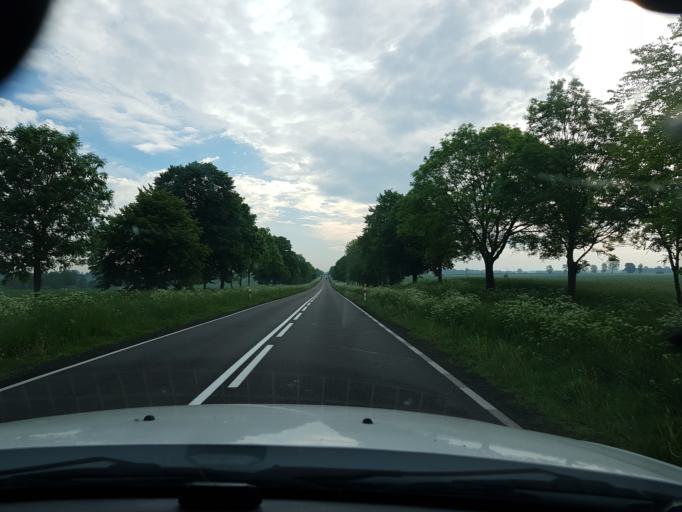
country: PL
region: West Pomeranian Voivodeship
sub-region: Powiat stargardzki
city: Stara Dabrowa
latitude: 53.3728
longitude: 15.1364
